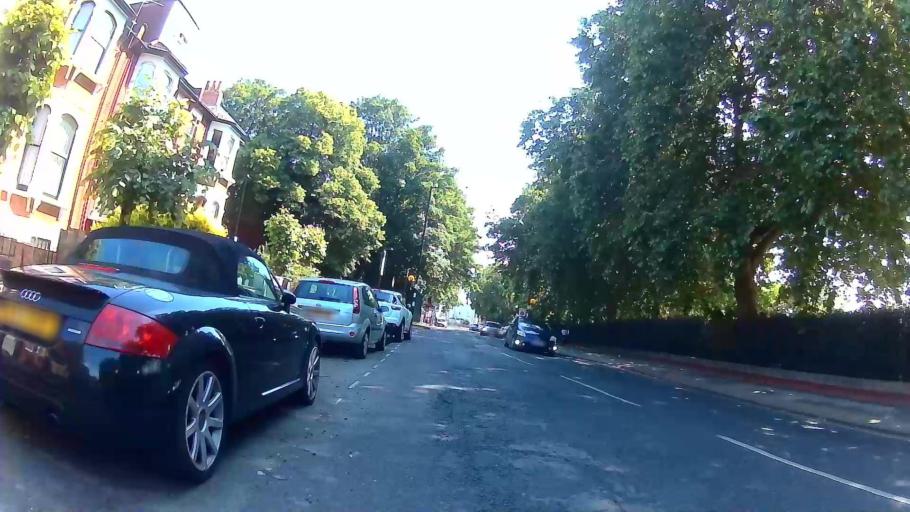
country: GB
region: England
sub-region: Greater London
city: East Ham
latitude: 51.5400
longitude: 0.0230
